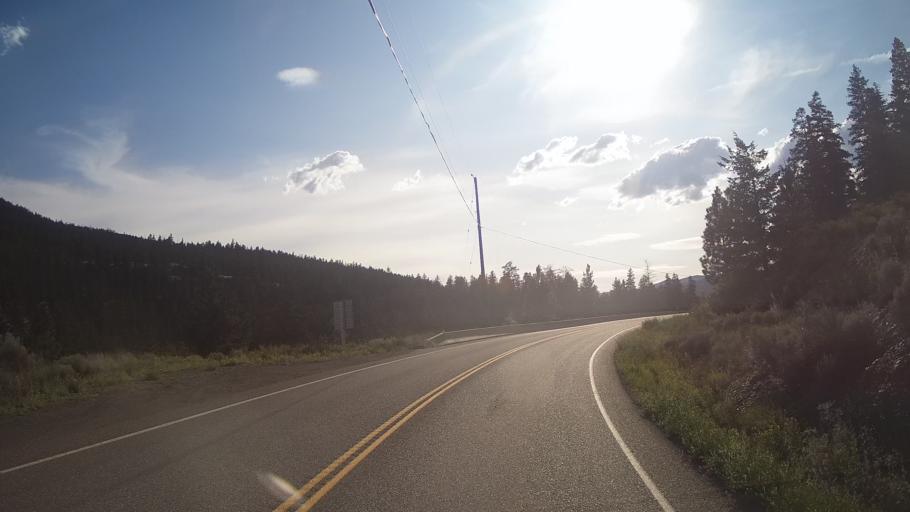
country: CA
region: British Columbia
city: Cache Creek
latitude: 50.8841
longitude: -121.4256
